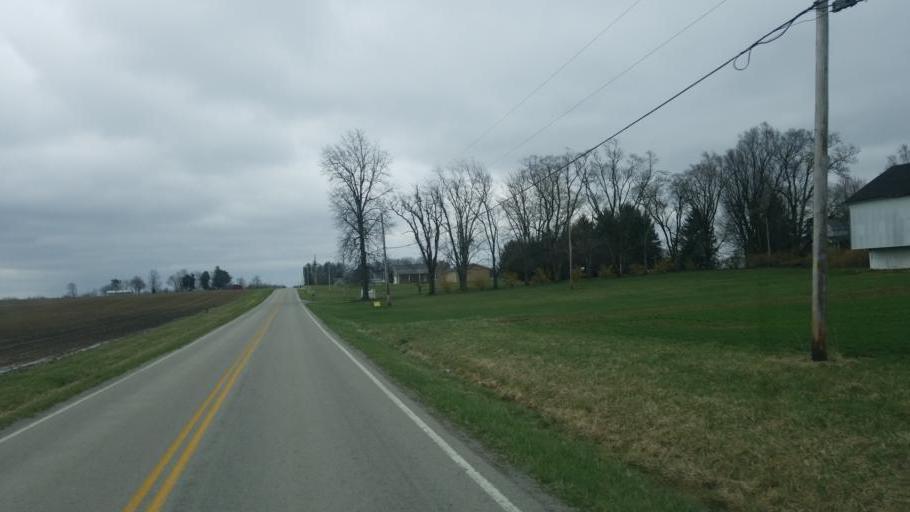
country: US
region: Ohio
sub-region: Wyandot County
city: Upper Sandusky
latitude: 40.8261
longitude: -83.1674
